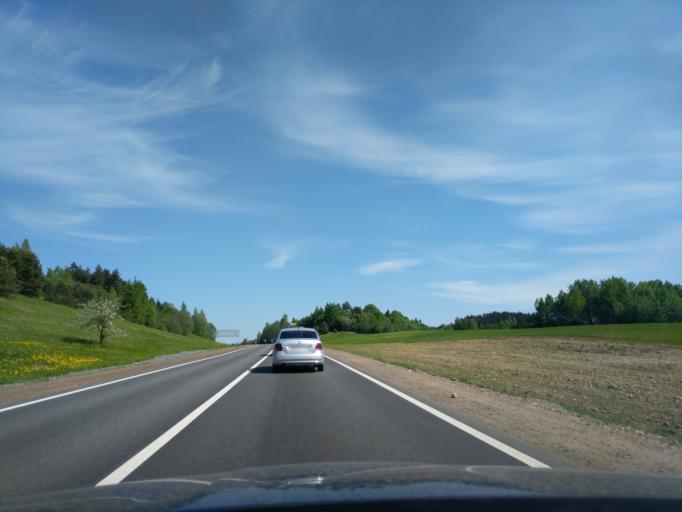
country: BY
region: Minsk
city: Bal'shavik
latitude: 54.0929
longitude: 27.5353
